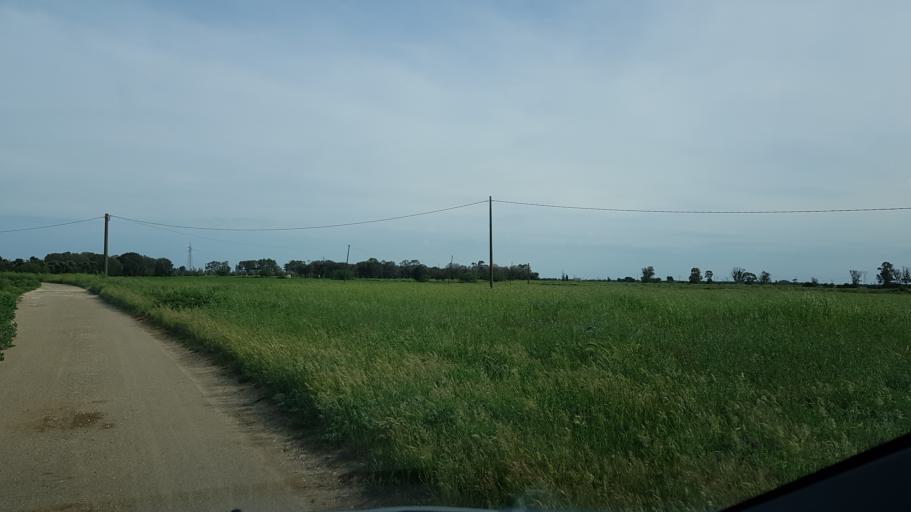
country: IT
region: Apulia
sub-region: Provincia di Brindisi
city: Tuturano
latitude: 40.5521
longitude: 17.9313
